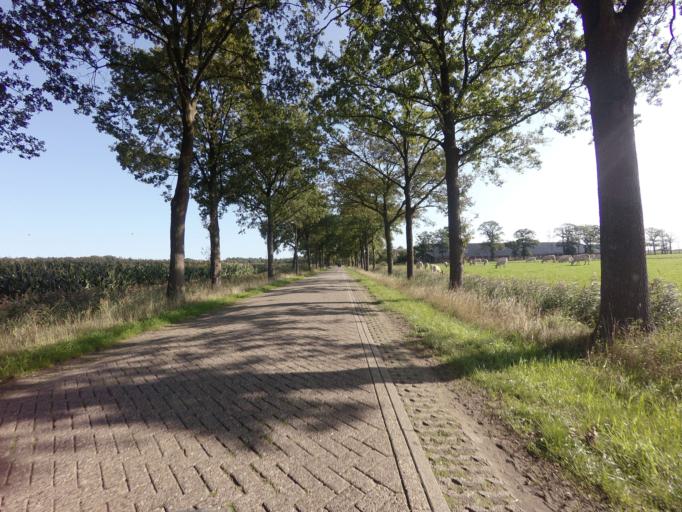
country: NL
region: Overijssel
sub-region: Gemeente Raalte
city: Raalte
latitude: 52.4224
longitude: 6.2931
